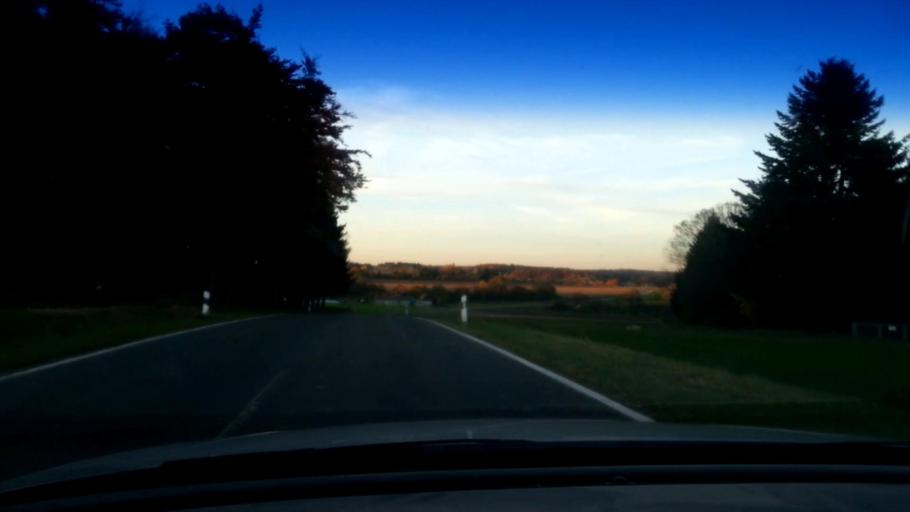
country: DE
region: Bavaria
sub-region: Upper Franconia
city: Heiligenstadt
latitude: 49.8497
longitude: 11.1167
